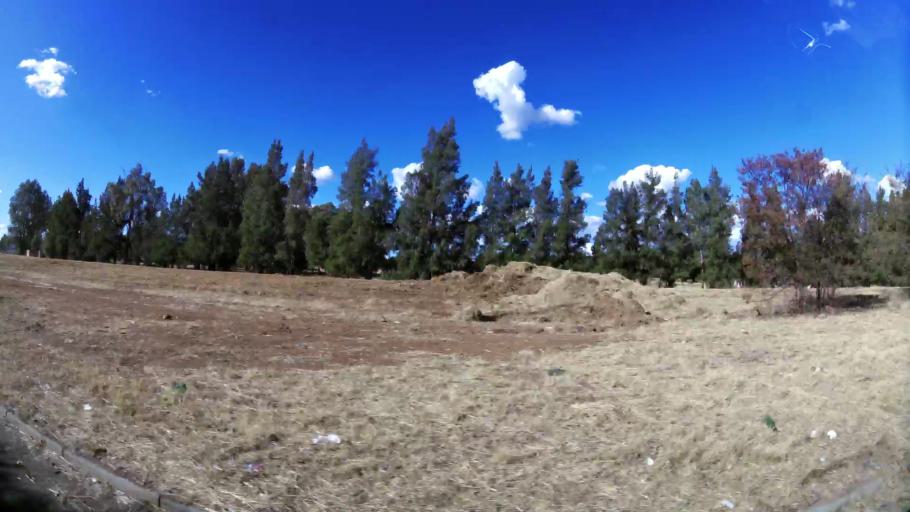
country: ZA
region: North-West
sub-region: Dr Kenneth Kaunda District Municipality
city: Klerksdorp
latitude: -26.8191
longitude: 26.6658
